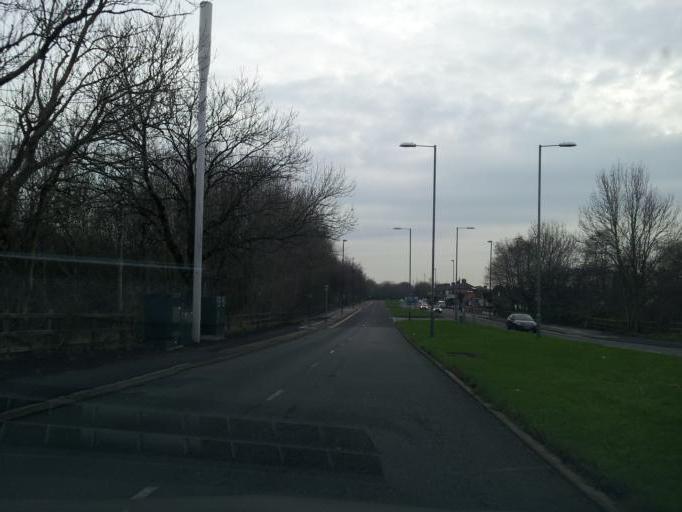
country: GB
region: England
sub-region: Manchester
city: Failsworth
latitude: 53.5139
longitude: -2.1697
